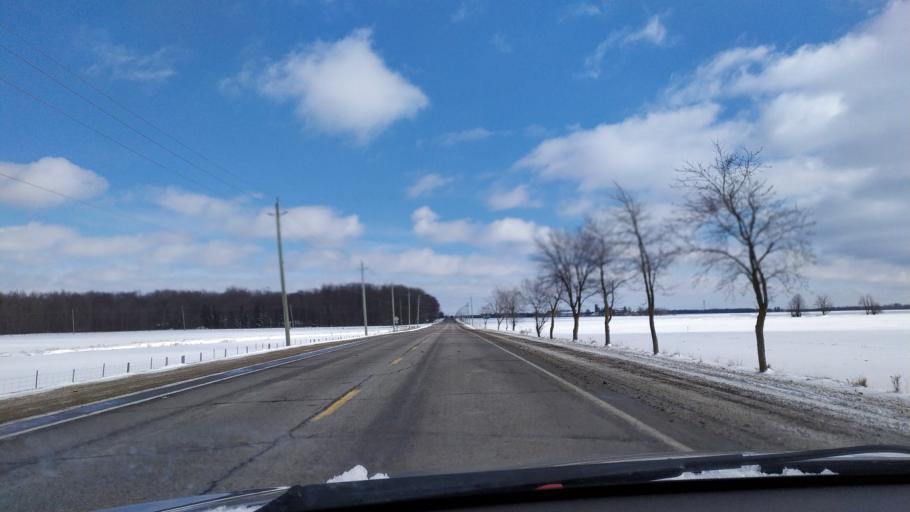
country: CA
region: Ontario
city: Waterloo
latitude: 43.5791
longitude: -80.5941
